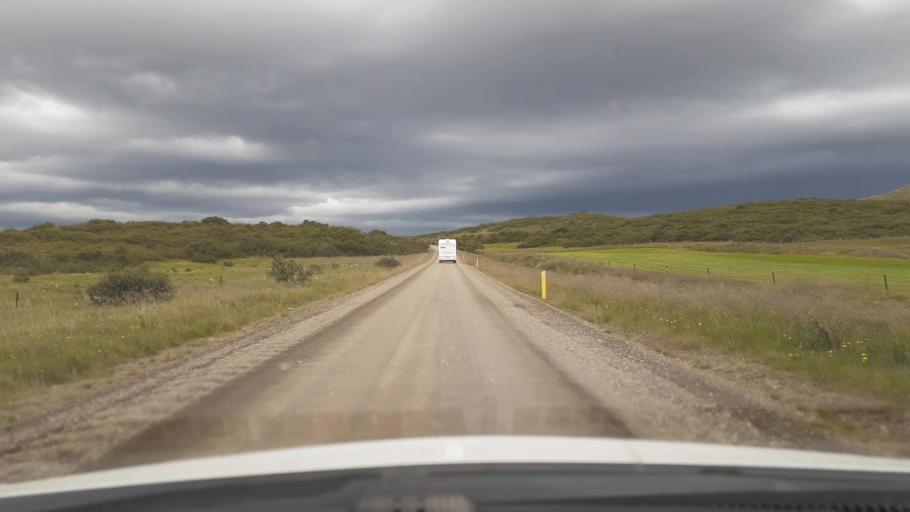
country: IS
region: West
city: Borgarnes
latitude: 64.5457
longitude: -21.6196
